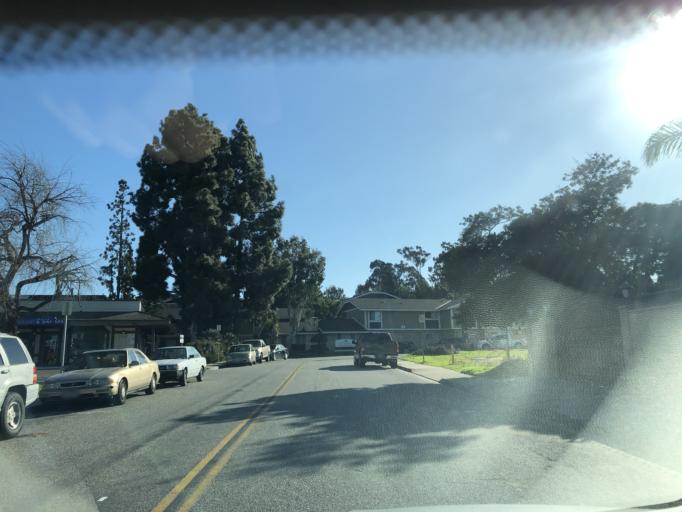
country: US
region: California
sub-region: San Diego County
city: Chula Vista
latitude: 32.6477
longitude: -117.0655
